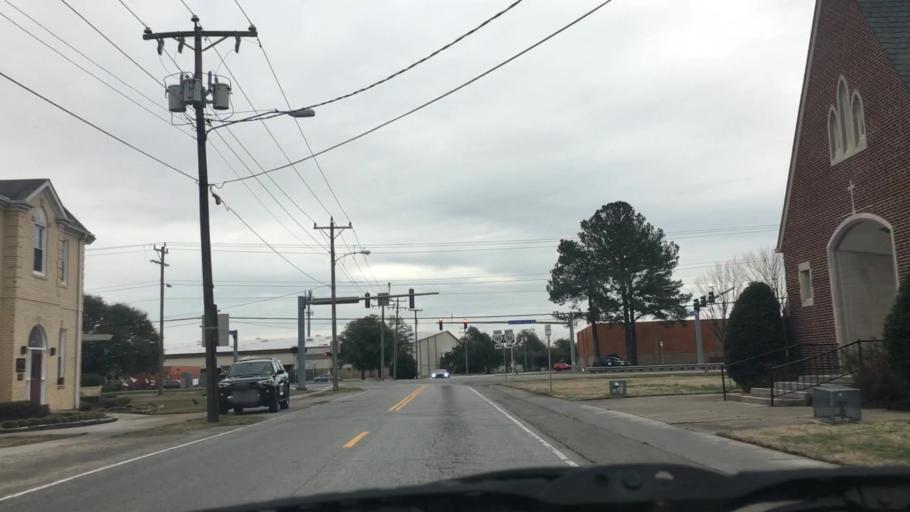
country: US
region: Virginia
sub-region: City of Norfolk
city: Norfolk
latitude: 36.8684
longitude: -76.2302
